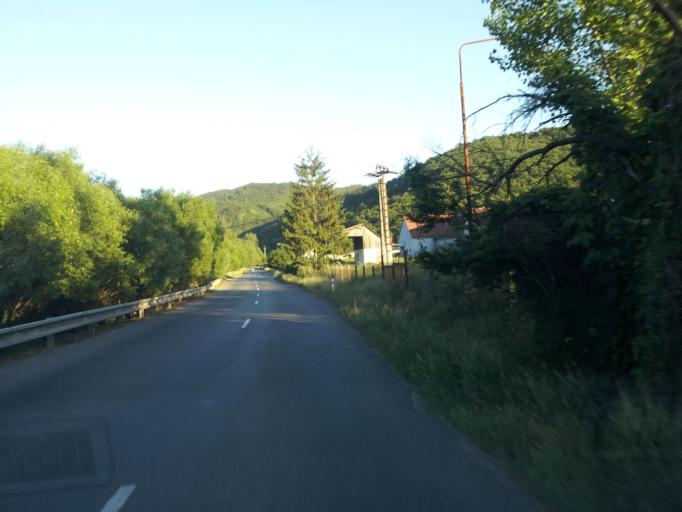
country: SK
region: Banskobystricky
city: Svaety Anton
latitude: 48.3506
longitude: 18.9285
